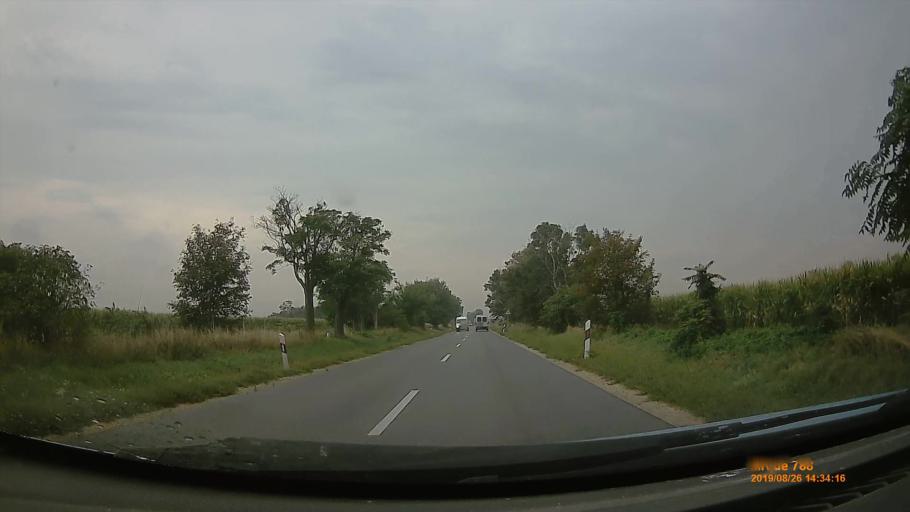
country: HU
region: Fejer
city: Zamoly
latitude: 47.2613
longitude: 18.4193
